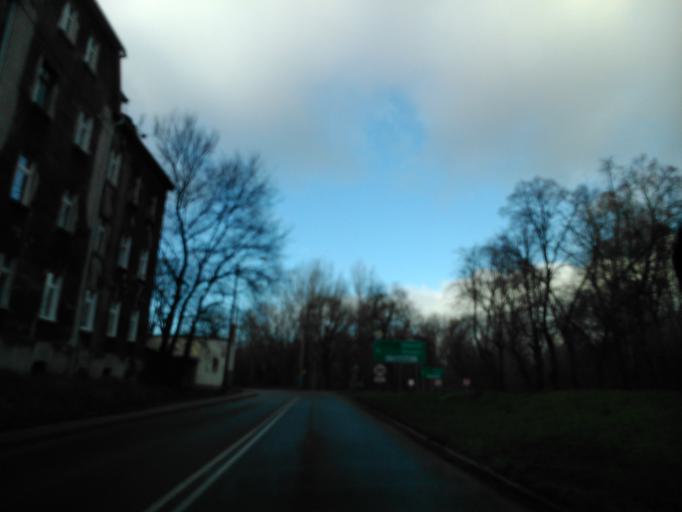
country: PL
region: Kujawsko-Pomorskie
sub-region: Torun
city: Torun
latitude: 53.0017
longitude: 18.6175
